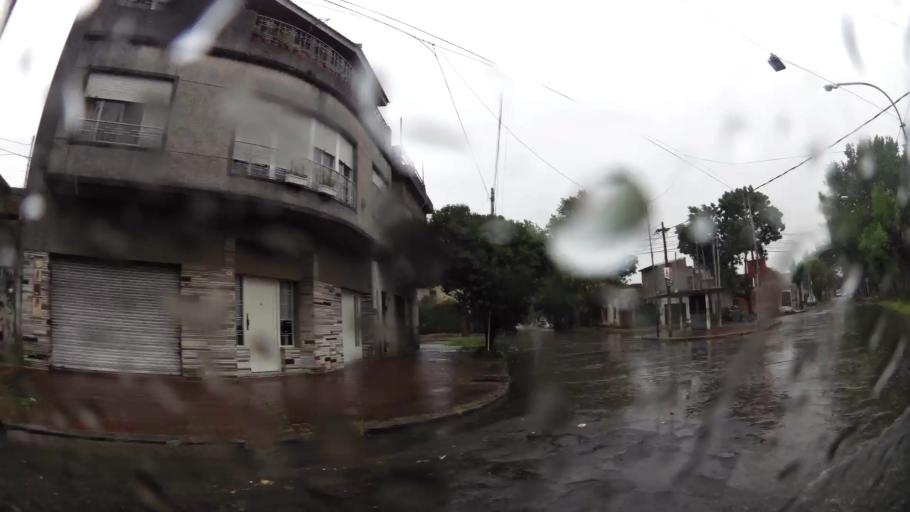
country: AR
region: Buenos Aires
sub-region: Partido de Lanus
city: Lanus
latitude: -34.7223
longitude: -58.3970
